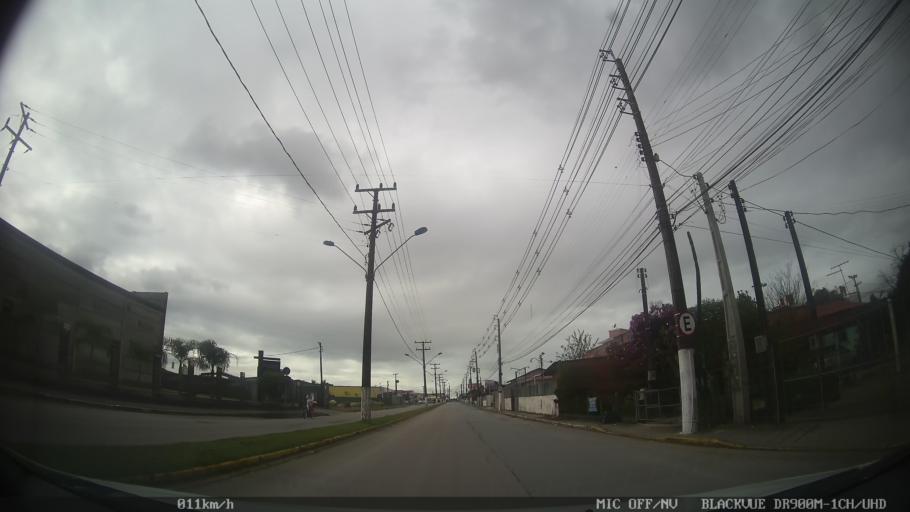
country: BR
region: Santa Catarina
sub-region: Biguacu
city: Biguacu
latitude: -27.5051
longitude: -48.6548
